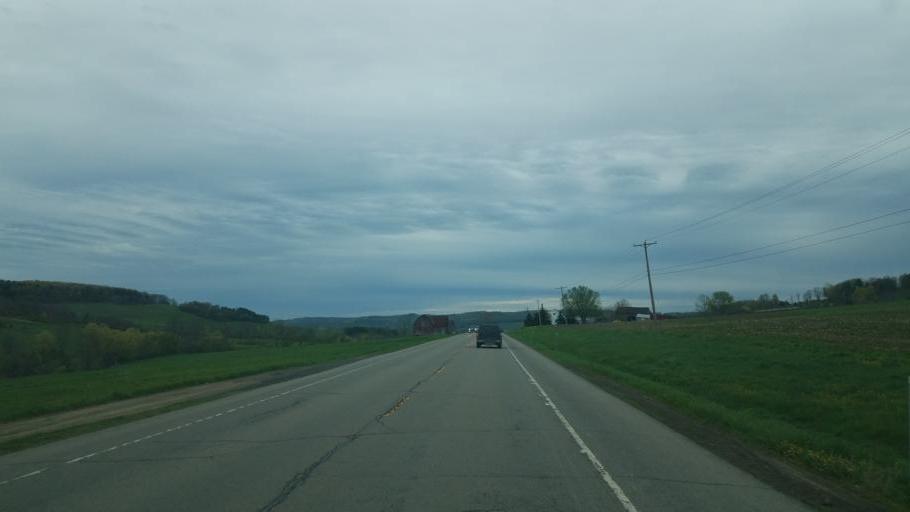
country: US
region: New York
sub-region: Steuben County
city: Canisteo
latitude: 42.1508
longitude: -77.5188
